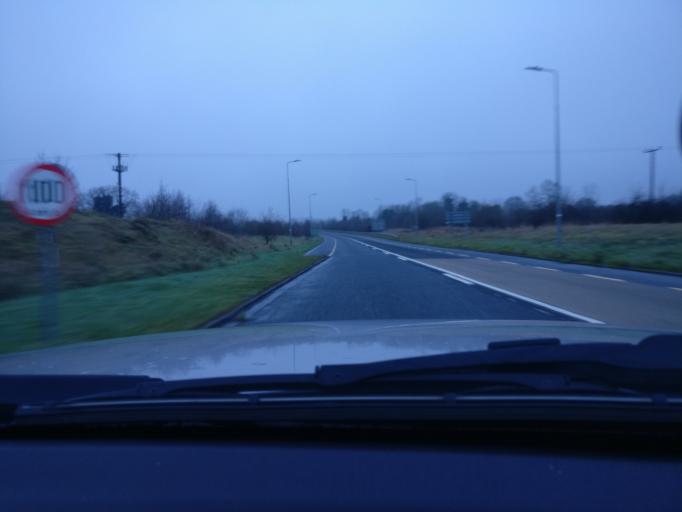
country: IE
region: Leinster
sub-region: An Iarmhi
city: Rochfortbridge
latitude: 53.3928
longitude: -7.3698
